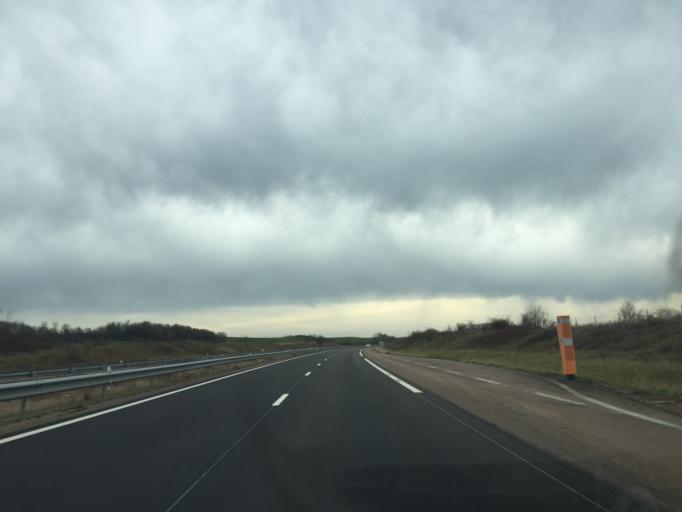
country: FR
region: Franche-Comte
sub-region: Departement du Jura
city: Bletterans
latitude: 46.7426
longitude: 5.5110
